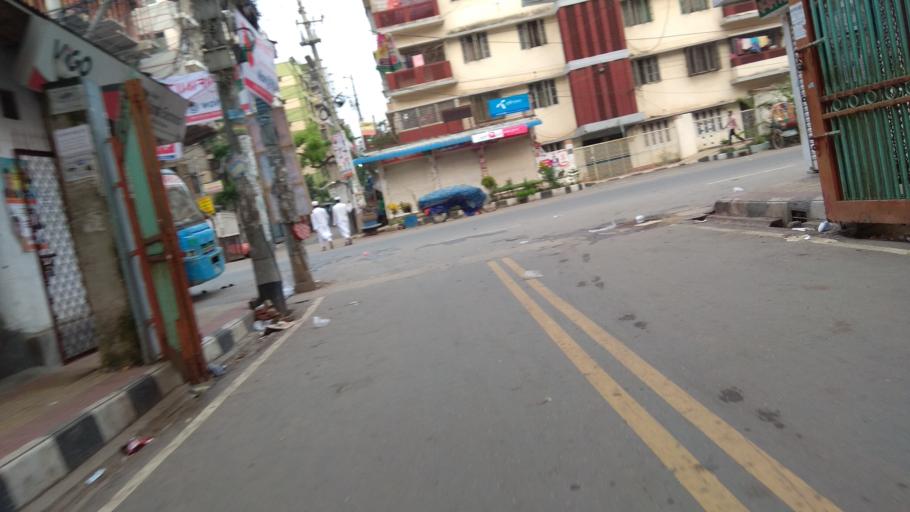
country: BD
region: Dhaka
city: Tungi
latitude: 23.8281
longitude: 90.3660
